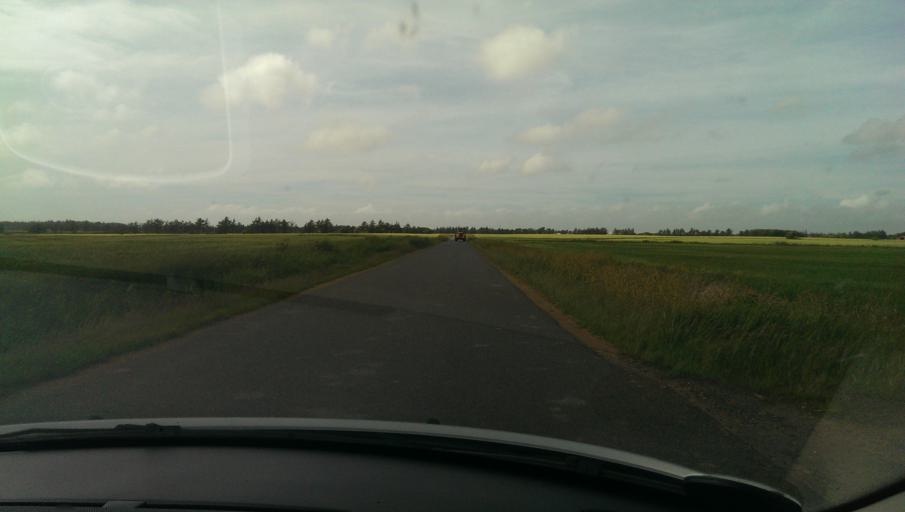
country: DK
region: Central Jutland
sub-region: Holstebro Kommune
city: Ulfborg
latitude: 56.2925
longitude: 8.2146
